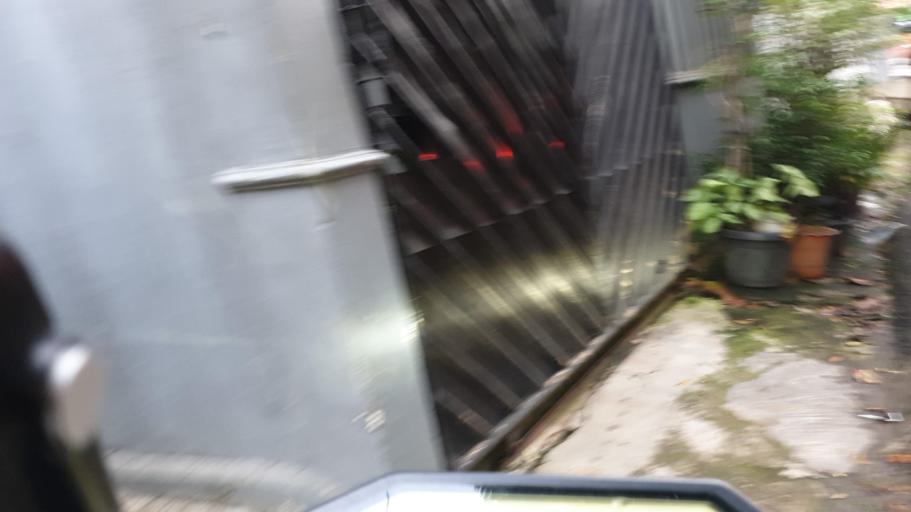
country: ID
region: West Java
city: Depok
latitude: -6.3449
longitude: 106.8242
